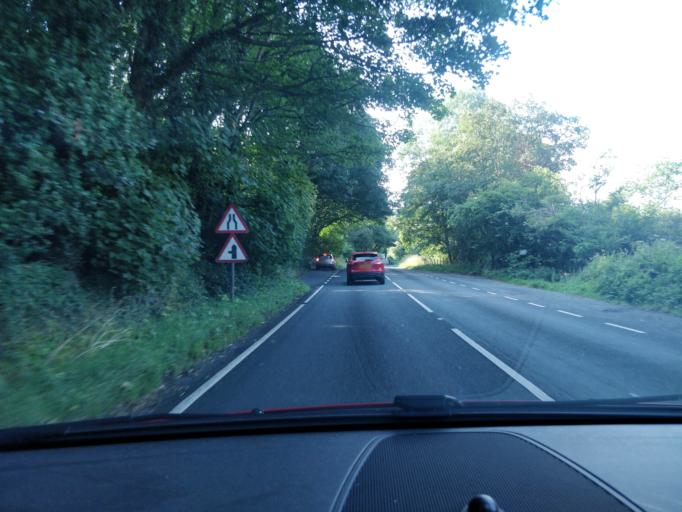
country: GB
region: Wales
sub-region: Conwy
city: Llanrwst
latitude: 53.1999
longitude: -3.8238
